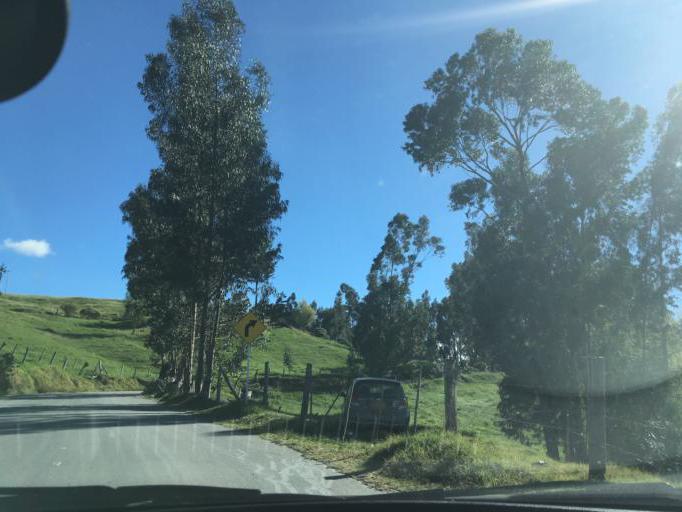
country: CO
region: Boyaca
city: Firavitoba
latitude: 5.5956
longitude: -72.9790
